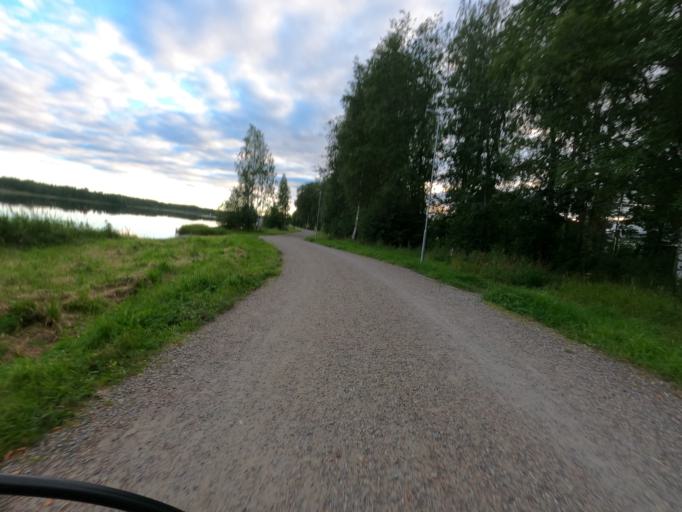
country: FI
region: North Karelia
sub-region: Joensuu
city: Joensuu
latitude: 62.6107
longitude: 29.8382
